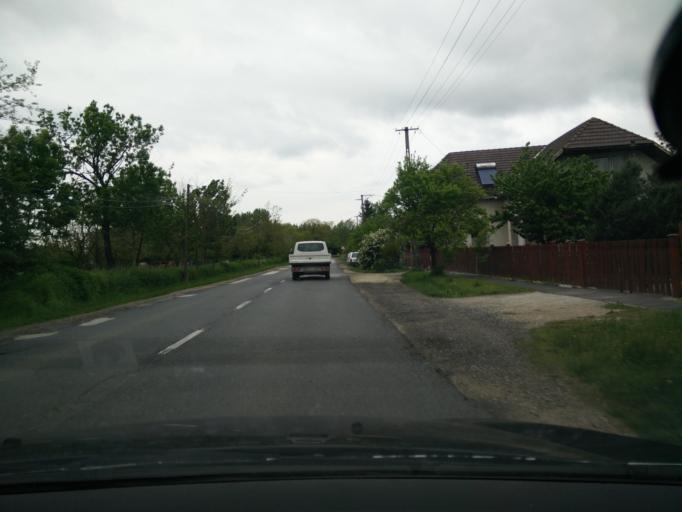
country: HU
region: Veszprem
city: Papa
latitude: 47.4025
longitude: 17.4679
